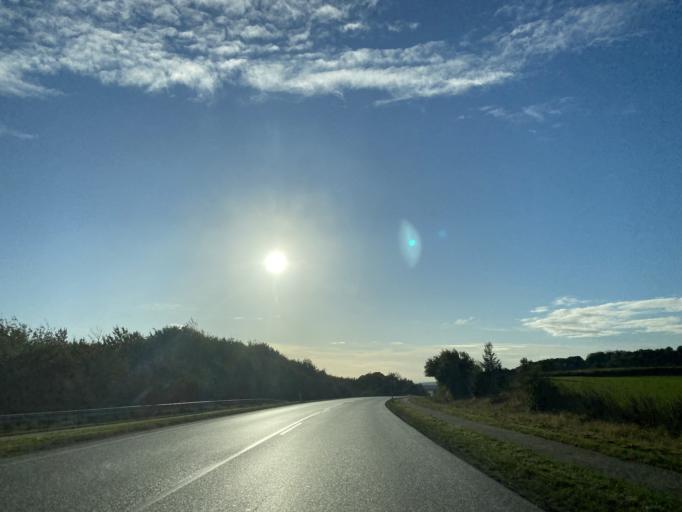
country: DK
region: Central Jutland
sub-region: Horsens Kommune
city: Horsens
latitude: 55.9032
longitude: 9.7440
